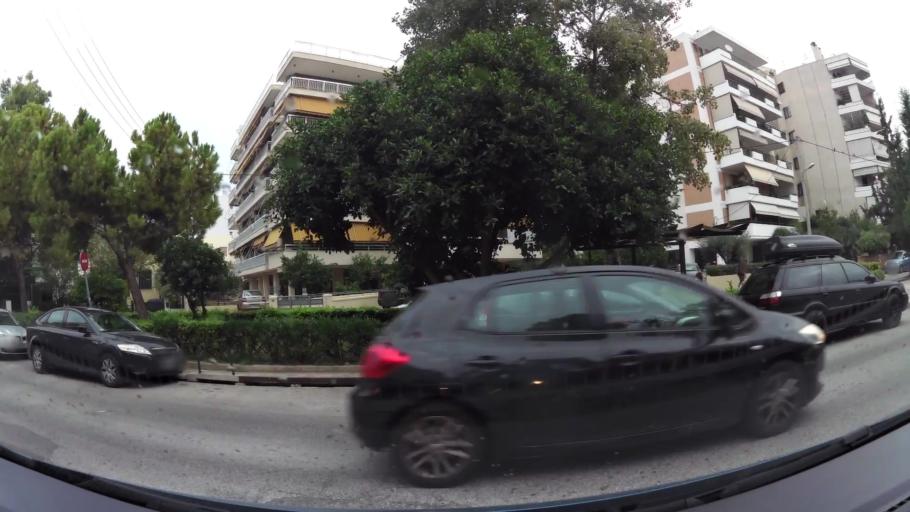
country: GR
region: Attica
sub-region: Nomarchia Athinas
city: Palaio Faliro
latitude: 37.9200
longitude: 23.7085
